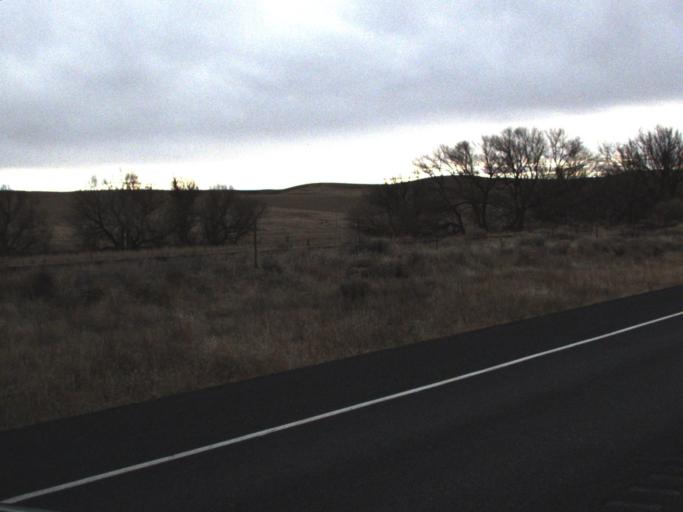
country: US
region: Washington
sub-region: Columbia County
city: Dayton
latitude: 46.7666
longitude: -117.9749
